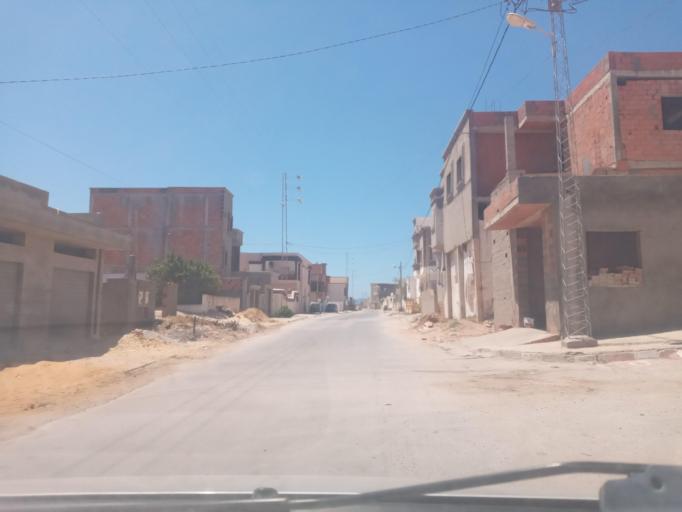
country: TN
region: Nabul
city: El Haouaria
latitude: 37.0499
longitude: 11.0029
